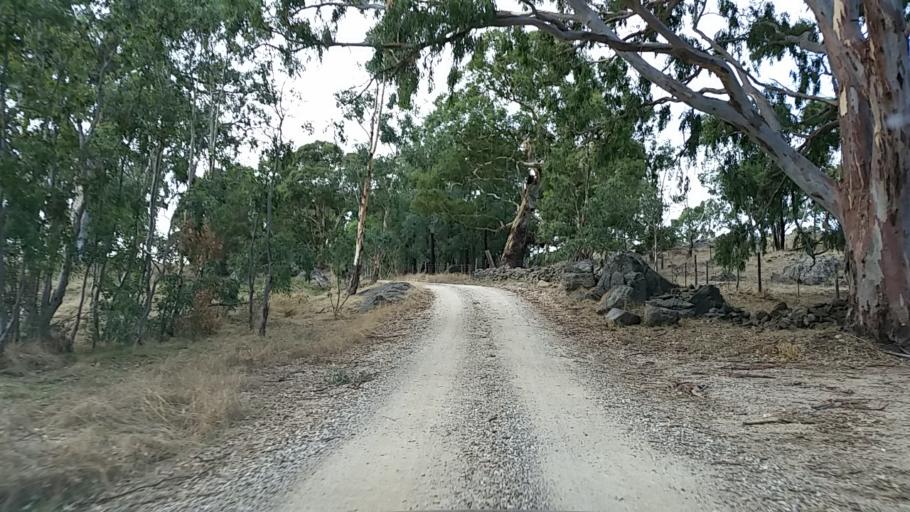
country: AU
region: South Australia
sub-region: Barossa
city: Angaston
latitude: -34.5692
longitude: 139.0742
